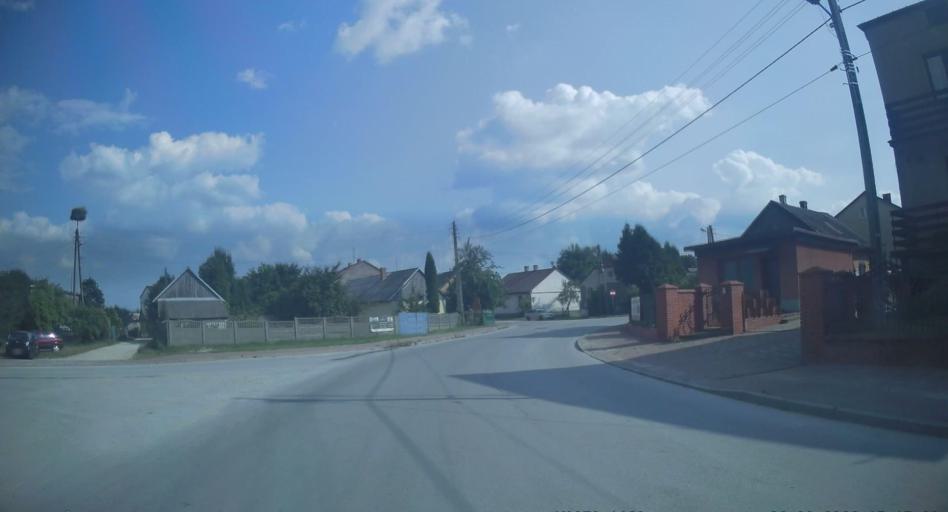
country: PL
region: Swietokrzyskie
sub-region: Powiat konecki
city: Radoszyce
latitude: 51.0768
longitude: 20.2571
